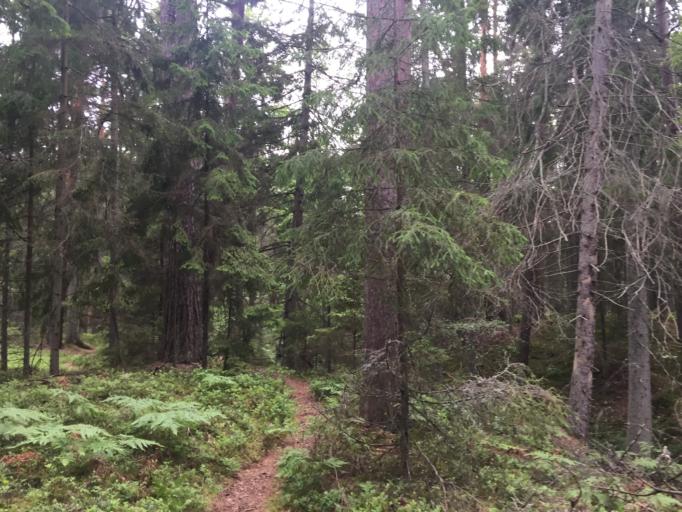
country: LV
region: Tukuma Rajons
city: Engure
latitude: 57.1288
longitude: 23.2324
